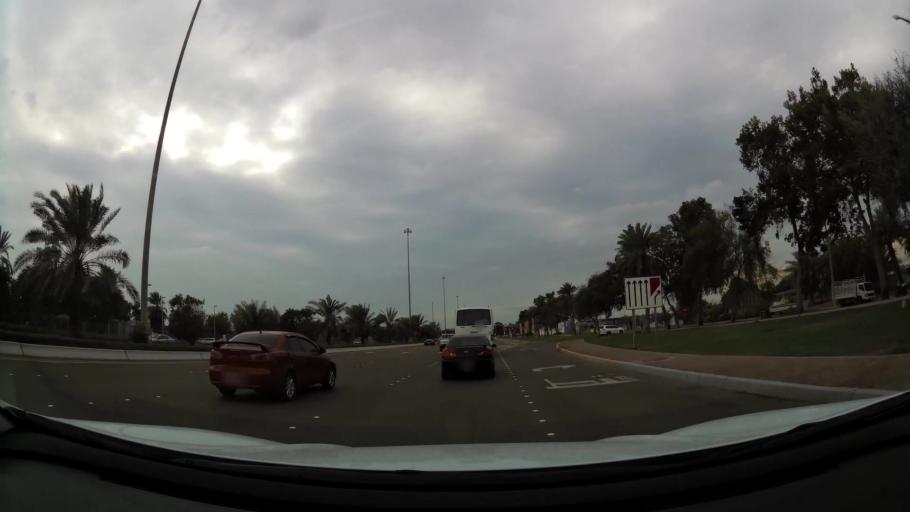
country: AE
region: Abu Dhabi
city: Abu Dhabi
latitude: 24.4286
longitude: 54.3959
